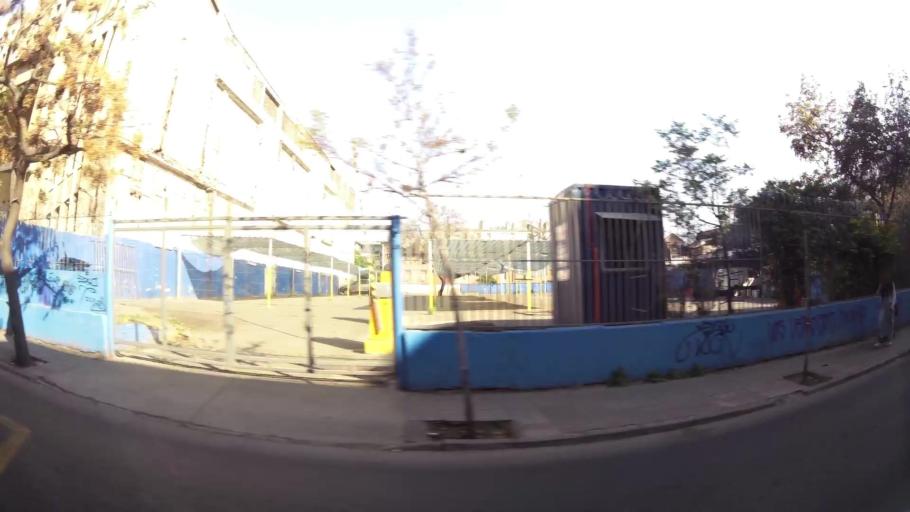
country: CL
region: Santiago Metropolitan
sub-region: Provincia de Santiago
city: Santiago
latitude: -33.4396
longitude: -70.6617
